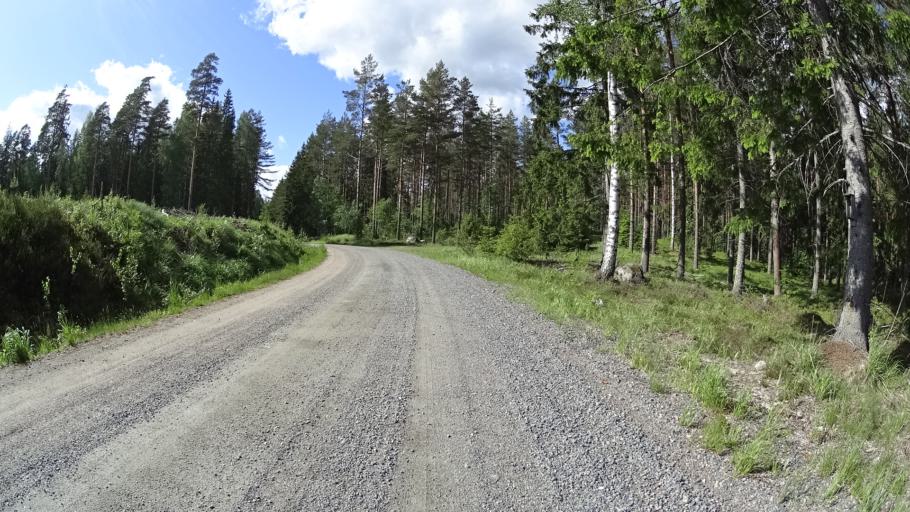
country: FI
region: Varsinais-Suomi
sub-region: Salo
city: Kisko
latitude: 60.1914
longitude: 23.5567
